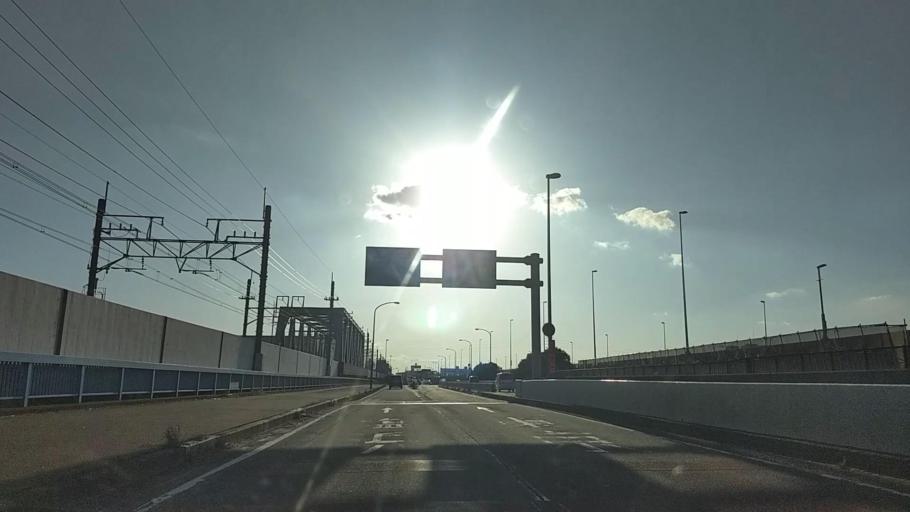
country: JP
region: Tokyo
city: Urayasu
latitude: 35.6762
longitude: 139.9324
